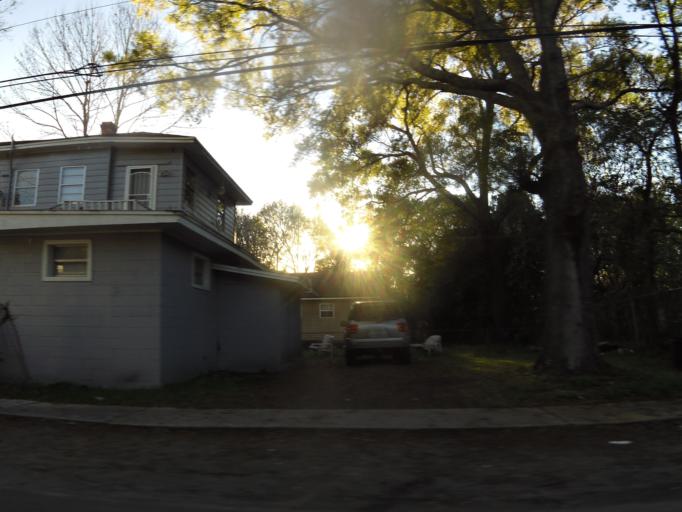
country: US
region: Florida
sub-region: Duval County
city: Jacksonville
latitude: 30.3347
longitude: -81.6970
